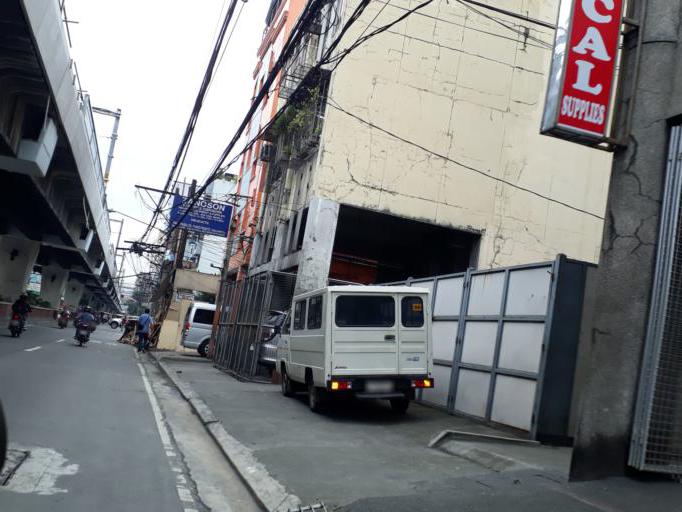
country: PH
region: Metro Manila
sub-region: City of Manila
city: Manila
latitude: 14.6097
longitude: 120.9824
